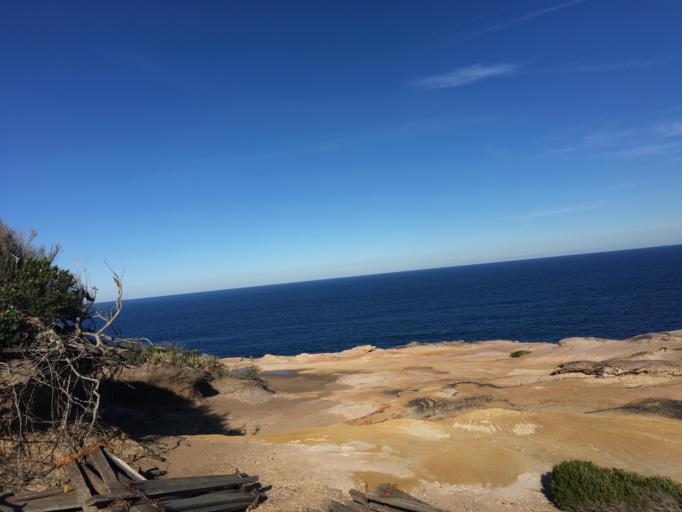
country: AU
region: New South Wales
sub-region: Sutherland Shire
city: Bundeena
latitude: -34.1265
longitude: 151.1327
